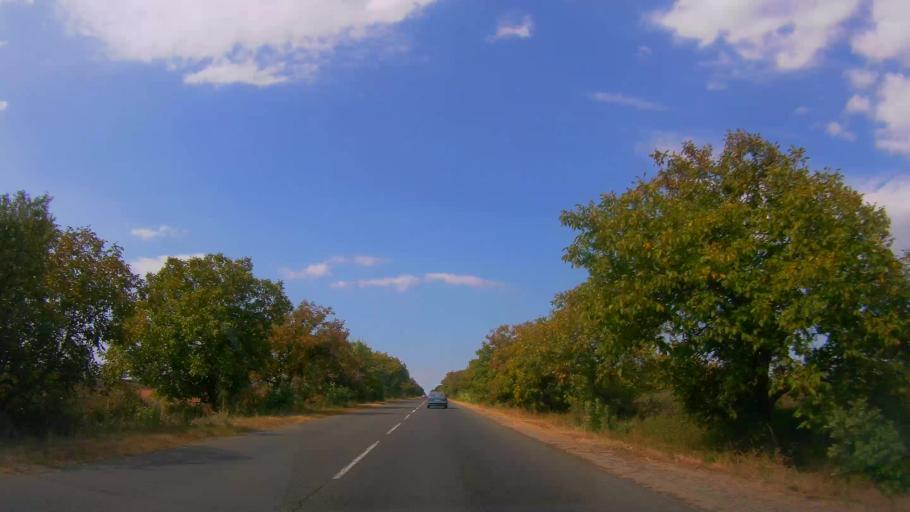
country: BG
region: Burgas
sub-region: Obshtina Aytos
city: Aytos
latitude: 42.6874
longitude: 27.1466
